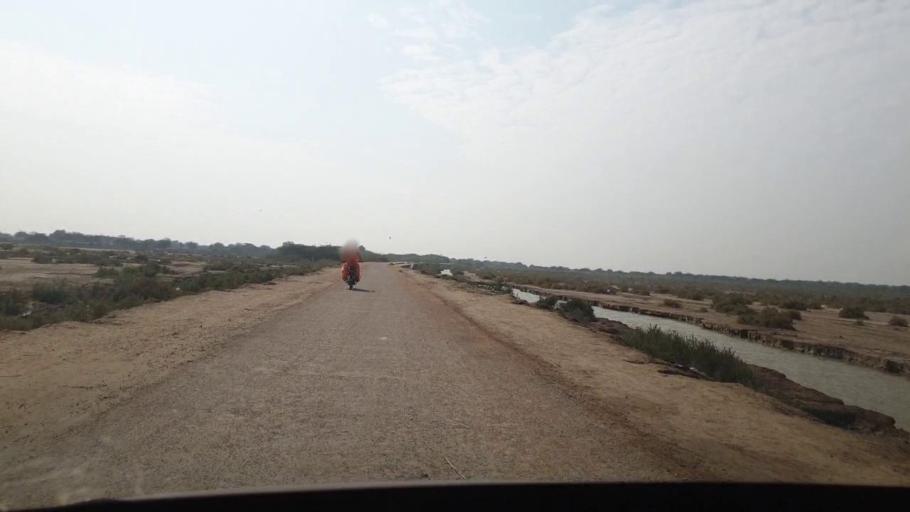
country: PK
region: Sindh
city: Chuhar Jamali
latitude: 24.2426
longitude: 67.9889
